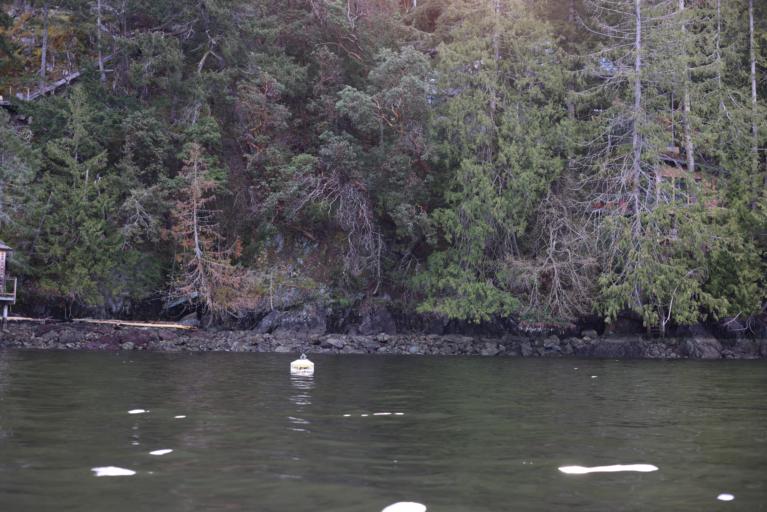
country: CA
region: British Columbia
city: Langford
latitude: 48.5659
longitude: -123.4953
